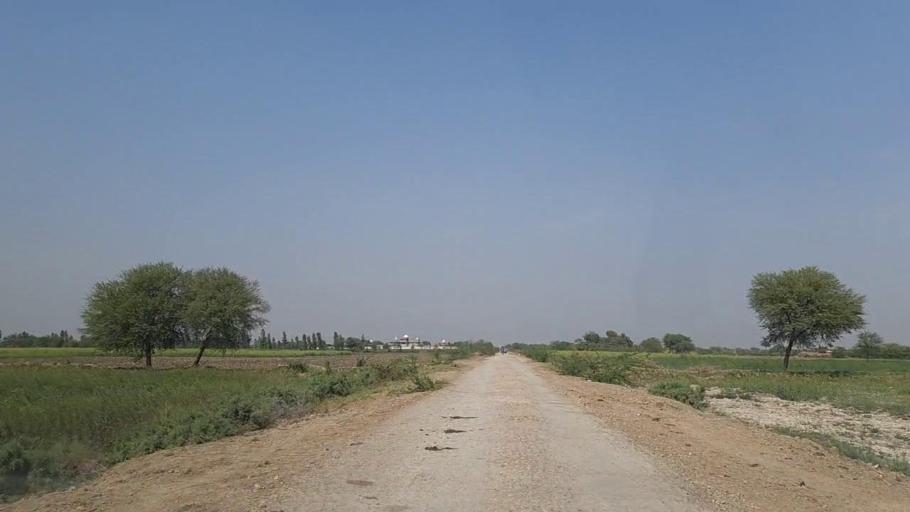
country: PK
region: Sindh
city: Samaro
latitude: 25.2622
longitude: 69.3947
